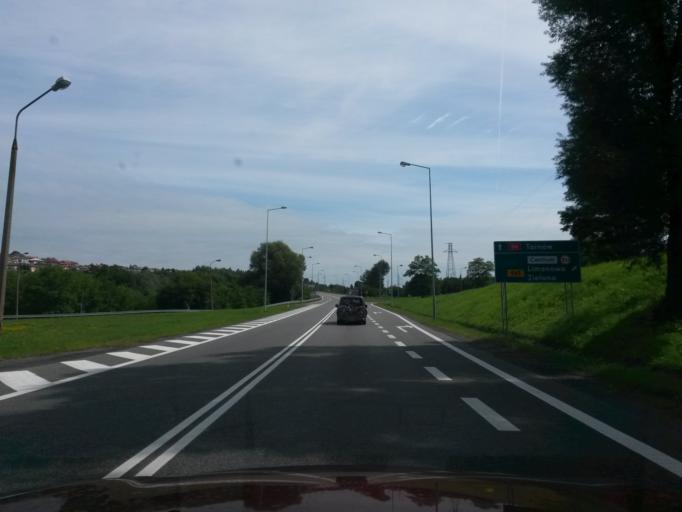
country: PL
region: Lesser Poland Voivodeship
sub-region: Powiat bochenski
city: Bochnia
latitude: 49.9582
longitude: 20.4283
